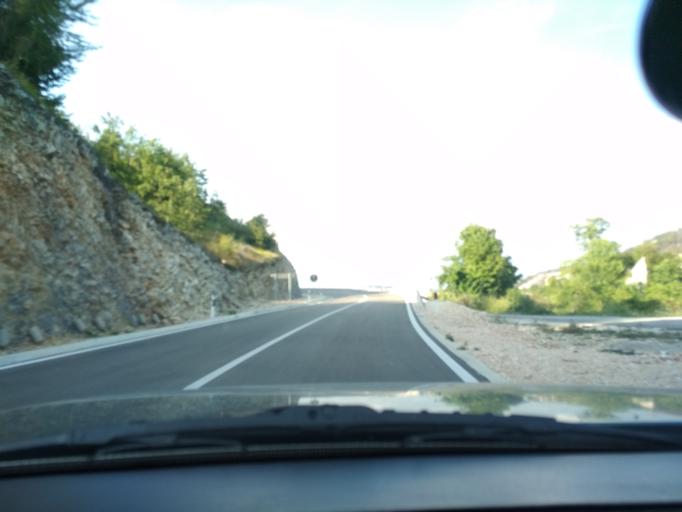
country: ME
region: Cetinje
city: Cetinje
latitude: 42.4350
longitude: 18.8575
